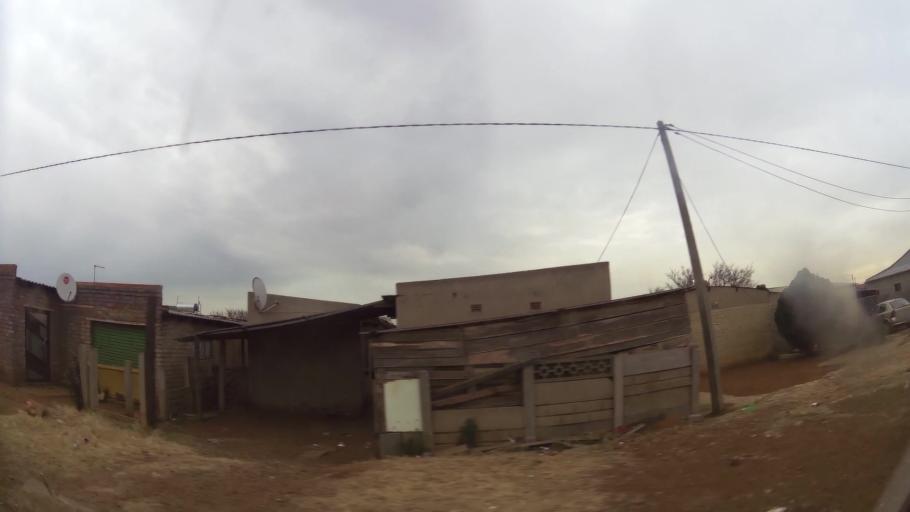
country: ZA
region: Gauteng
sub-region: Ekurhuleni Metropolitan Municipality
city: Germiston
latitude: -26.3812
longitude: 28.1733
